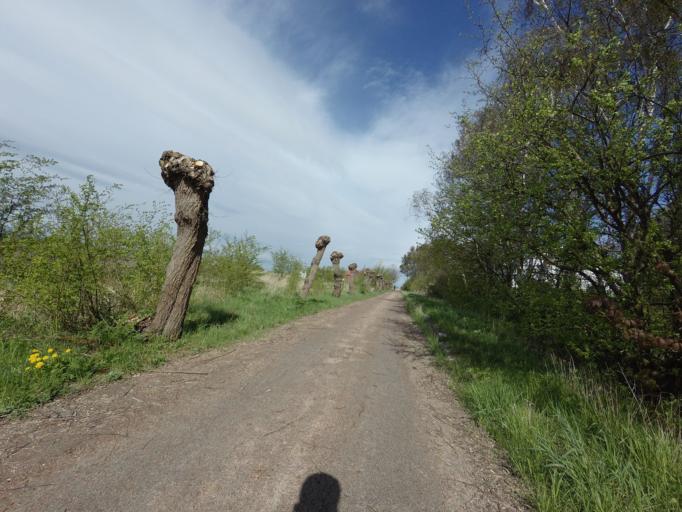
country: SE
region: Skane
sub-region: Malmo
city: Tygelsjo
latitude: 55.5263
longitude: 12.9855
